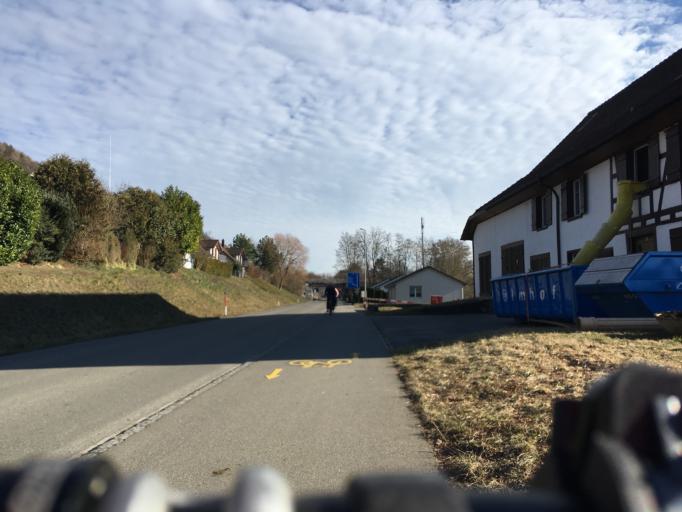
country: CH
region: Thurgau
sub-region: Frauenfeld District
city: Wagenhausen
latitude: 47.6754
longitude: 8.8335
